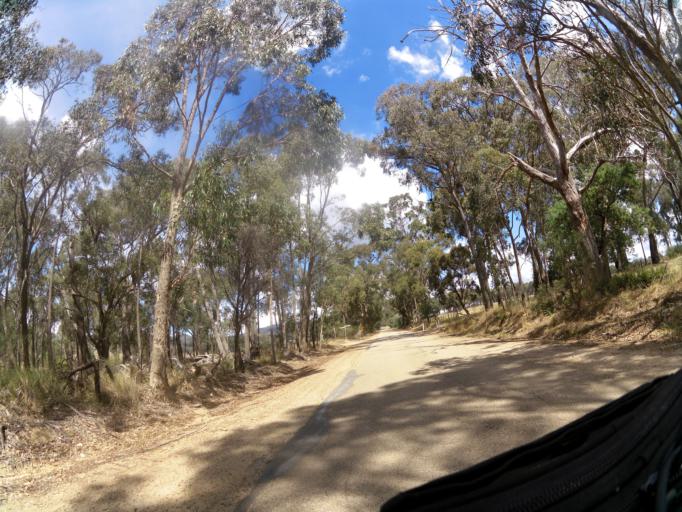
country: AU
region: Victoria
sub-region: Benalla
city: Benalla
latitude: -36.7775
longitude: 145.9736
